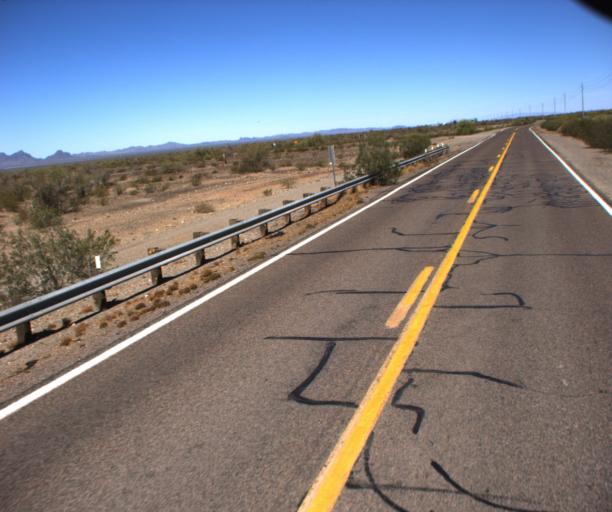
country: US
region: Arizona
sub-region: La Paz County
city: Salome
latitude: 33.7675
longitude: -113.7898
